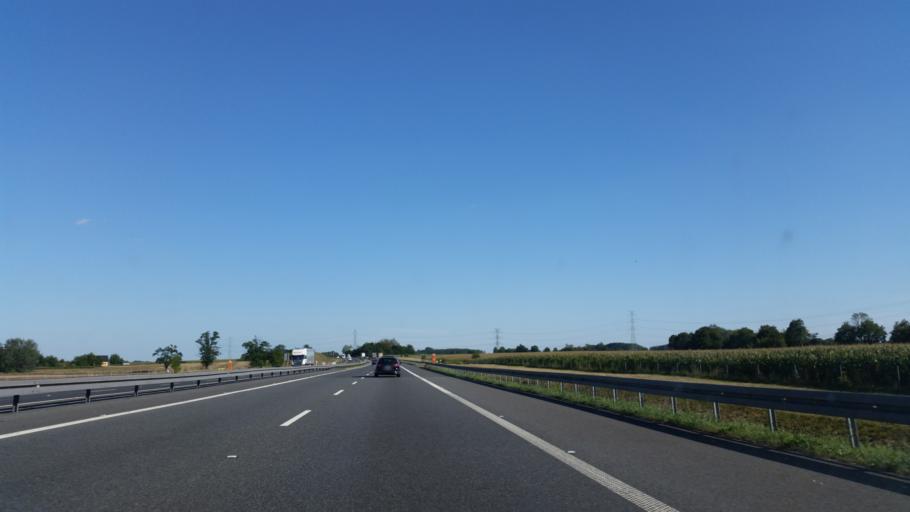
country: PL
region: Lower Silesian Voivodeship
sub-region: Powiat wroclawski
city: Zorawina
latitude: 50.9509
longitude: 17.0844
